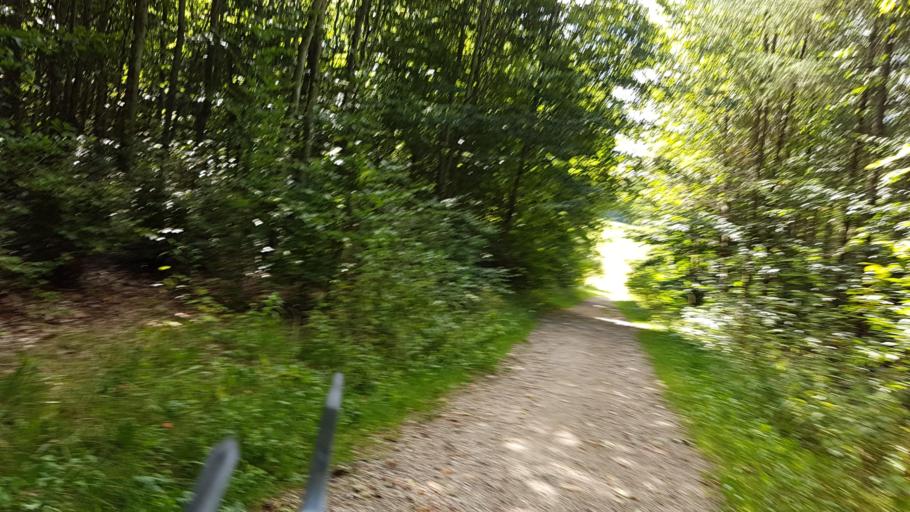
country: DK
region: Capital Region
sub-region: Egedal Kommune
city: Olstykke
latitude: 55.8056
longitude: 12.1667
